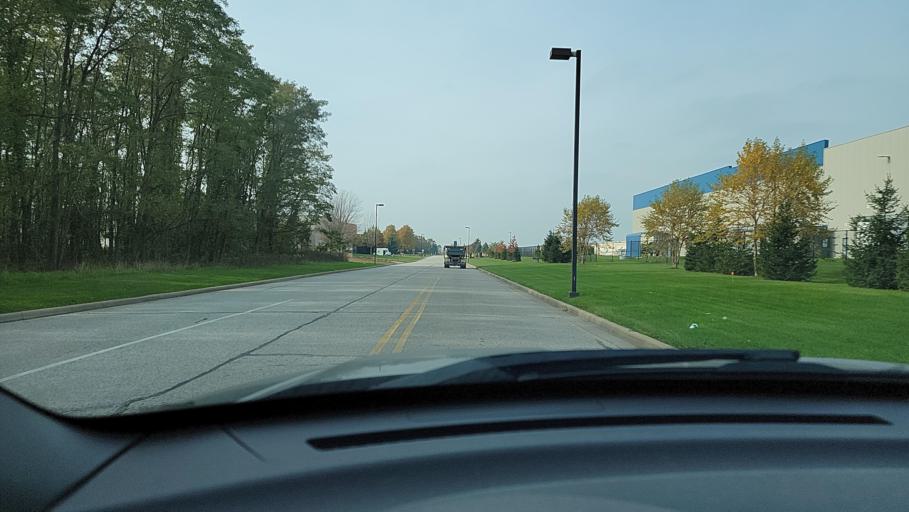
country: US
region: Indiana
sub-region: Porter County
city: Burns Harbor
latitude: 41.6056
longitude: -87.1563
